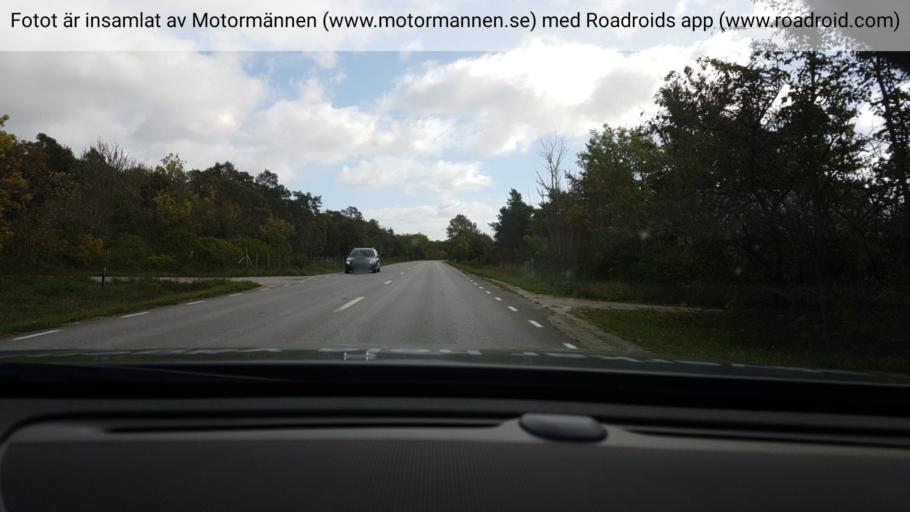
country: SE
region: Gotland
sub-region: Gotland
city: Slite
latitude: 57.8567
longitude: 19.0101
